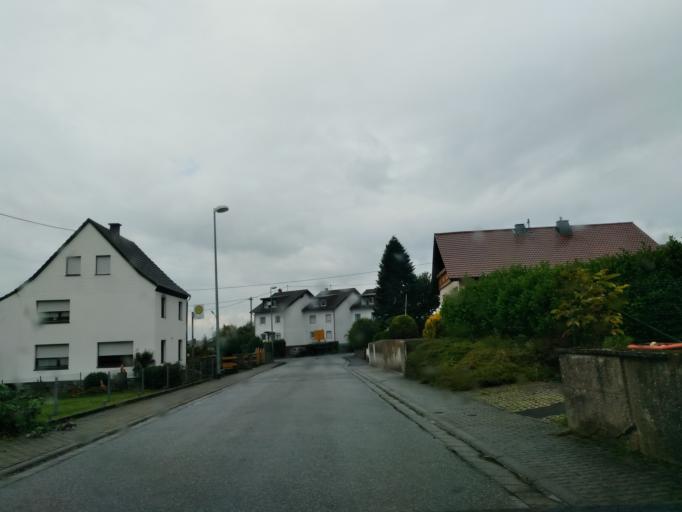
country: DE
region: Rheinland-Pfalz
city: Kircheib
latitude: 50.6848
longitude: 7.4474
